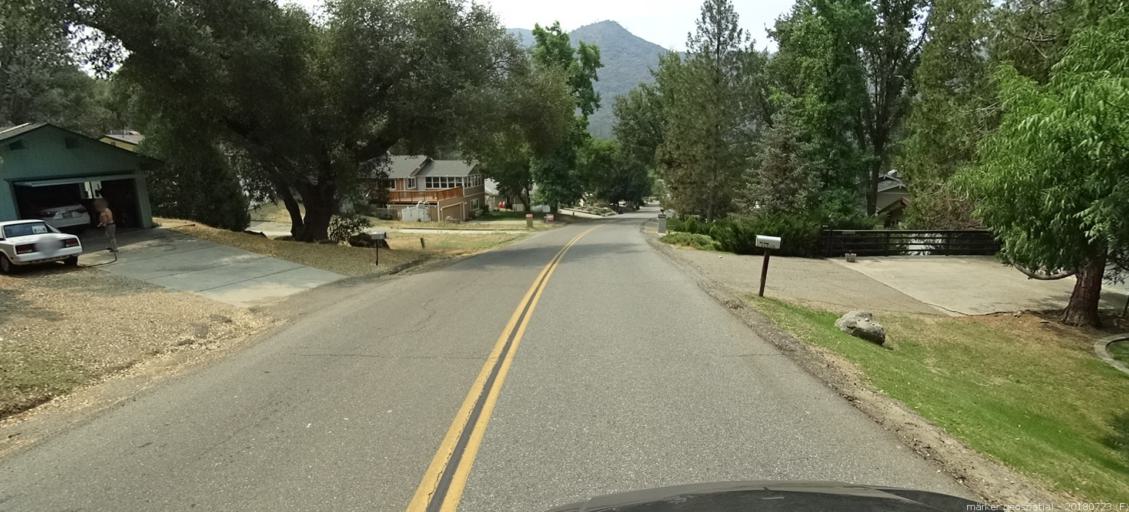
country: US
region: California
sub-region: Madera County
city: Ahwahnee
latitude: 37.3387
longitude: -119.7092
